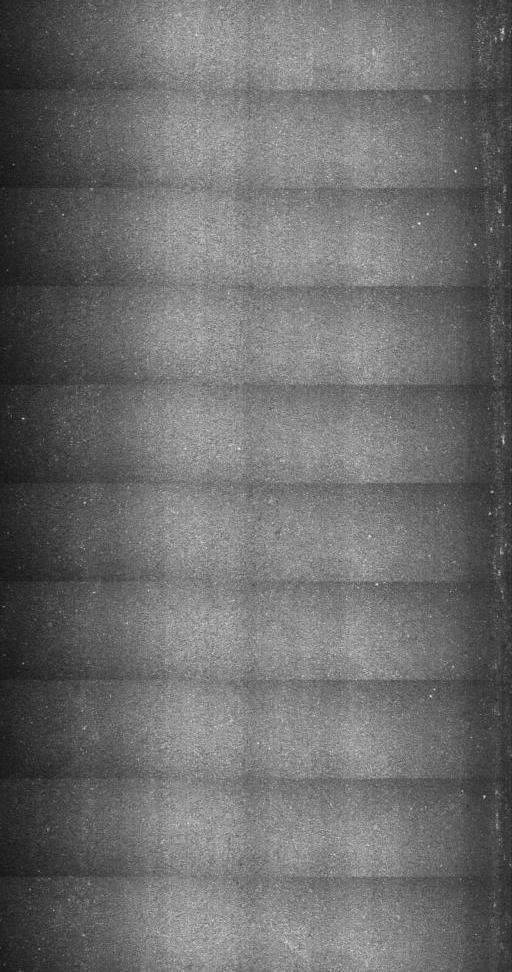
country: US
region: Vermont
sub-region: Franklin County
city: Richford
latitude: 44.9250
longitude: -72.6765
